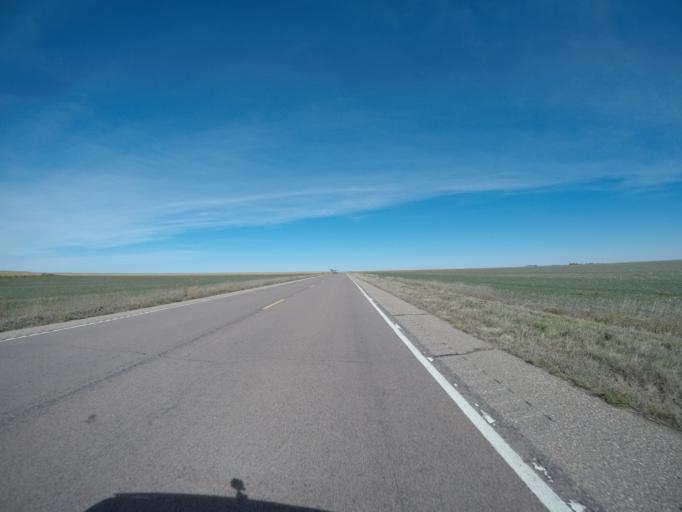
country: US
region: Colorado
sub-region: Kit Carson County
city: Burlington
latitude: 39.6623
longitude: -102.4305
